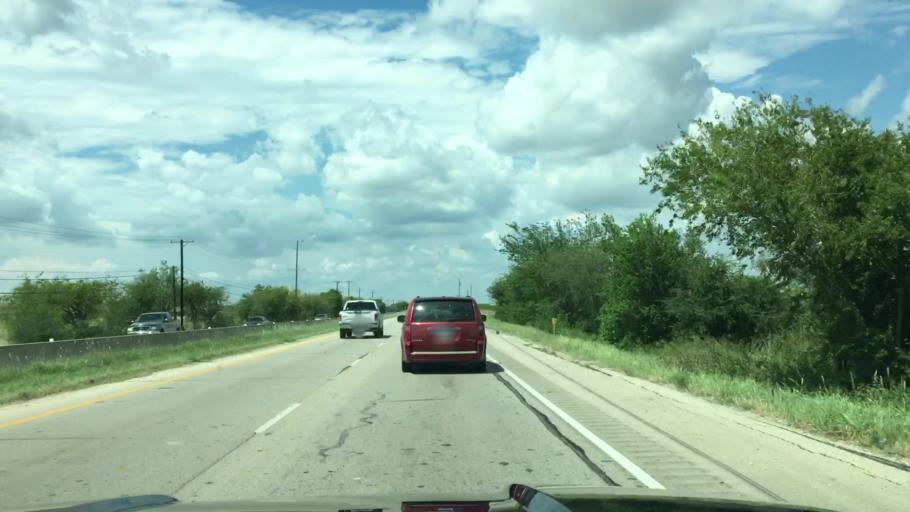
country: US
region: Texas
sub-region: Tarrant County
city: Saginaw
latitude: 32.8865
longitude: -97.3866
